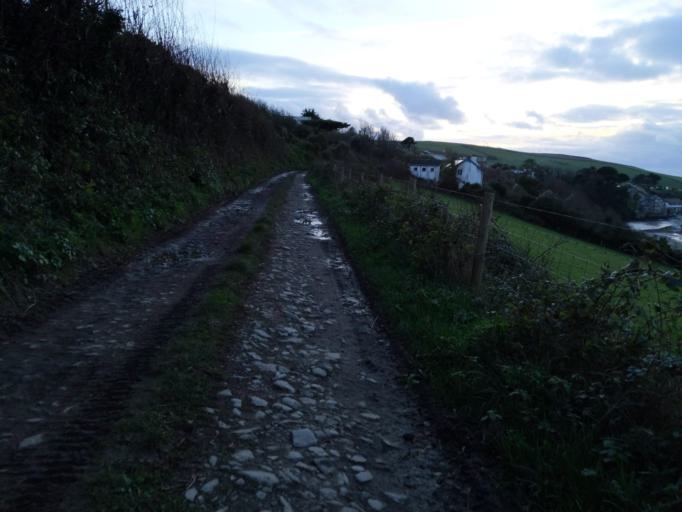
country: GB
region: England
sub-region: Devon
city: Modbury
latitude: 50.2810
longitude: -3.8650
